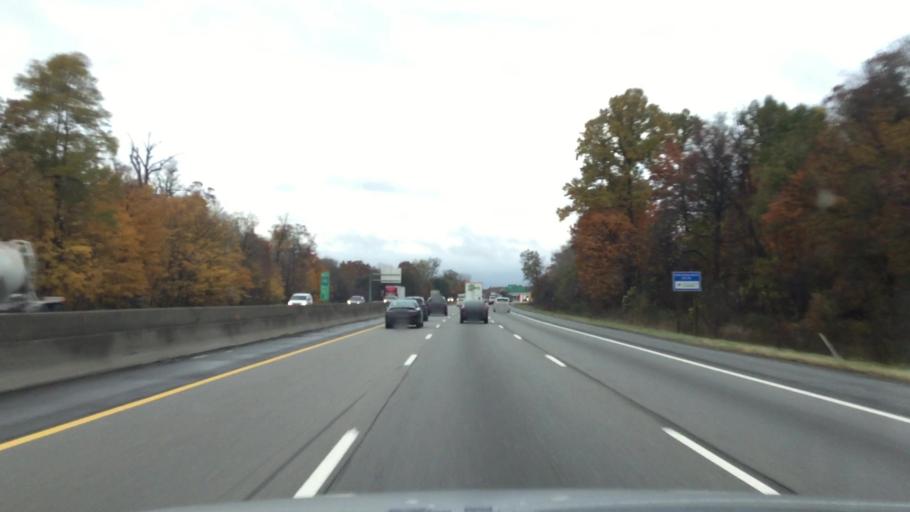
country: US
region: Michigan
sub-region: Washtenaw County
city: Ypsilanti
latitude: 42.2245
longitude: -83.6383
